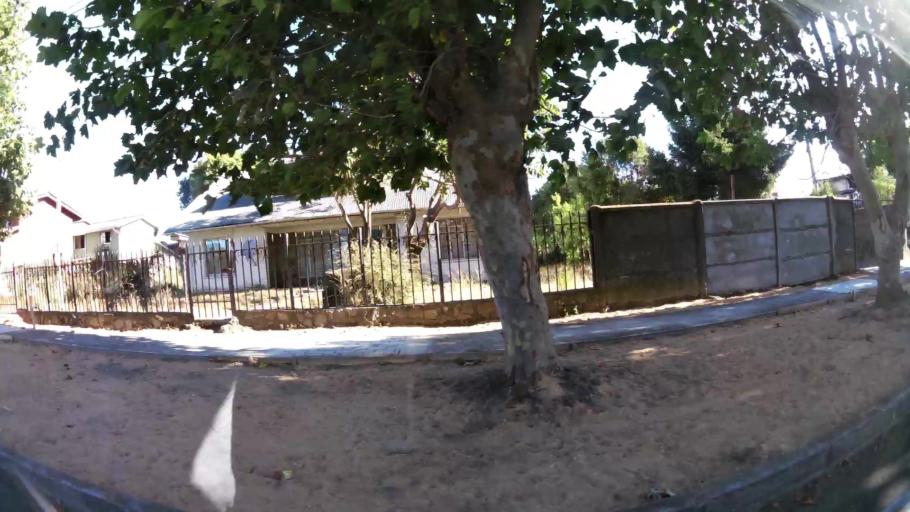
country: CL
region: Biobio
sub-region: Provincia de Concepcion
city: Concepcion
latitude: -36.8371
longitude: -73.1019
